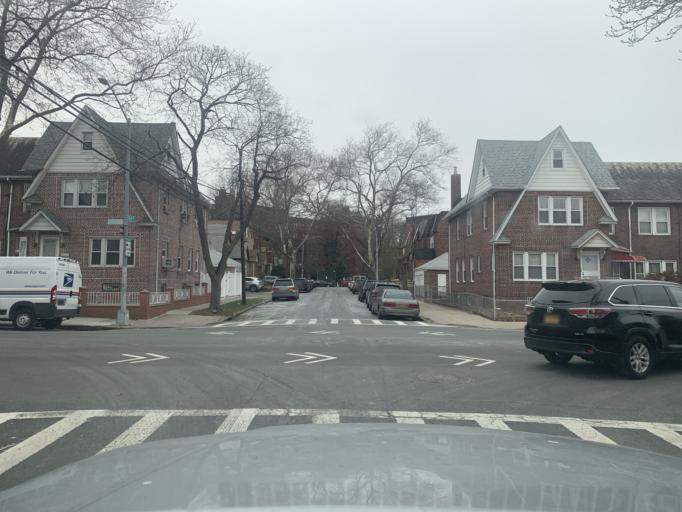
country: US
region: New York
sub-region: Queens County
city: Borough of Queens
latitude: 40.7238
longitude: -73.8705
